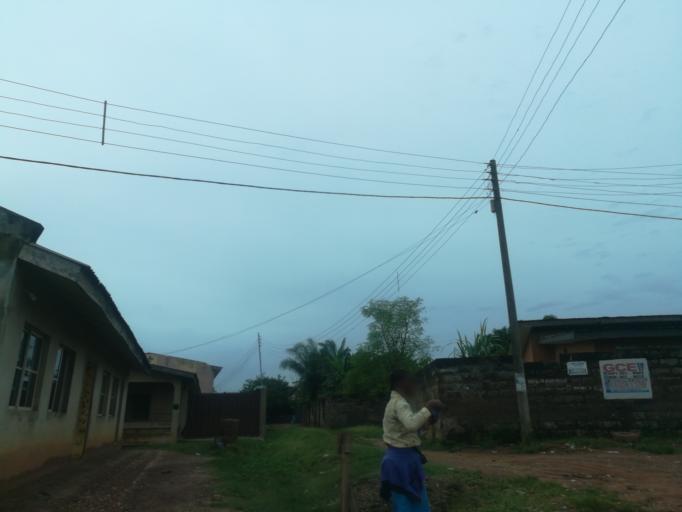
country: NG
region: Oyo
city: Egbeda
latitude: 7.3902
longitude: 3.9788
